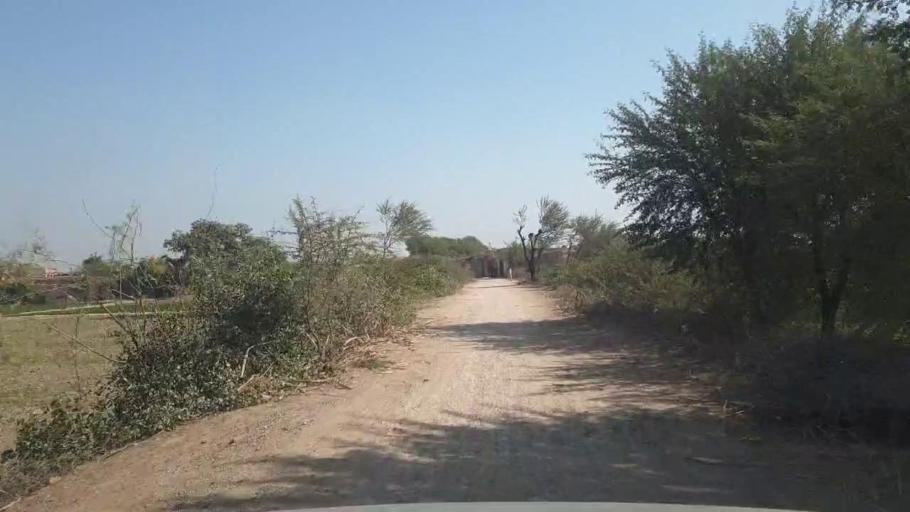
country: PK
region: Sindh
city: Chambar
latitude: 25.2910
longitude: 68.8285
